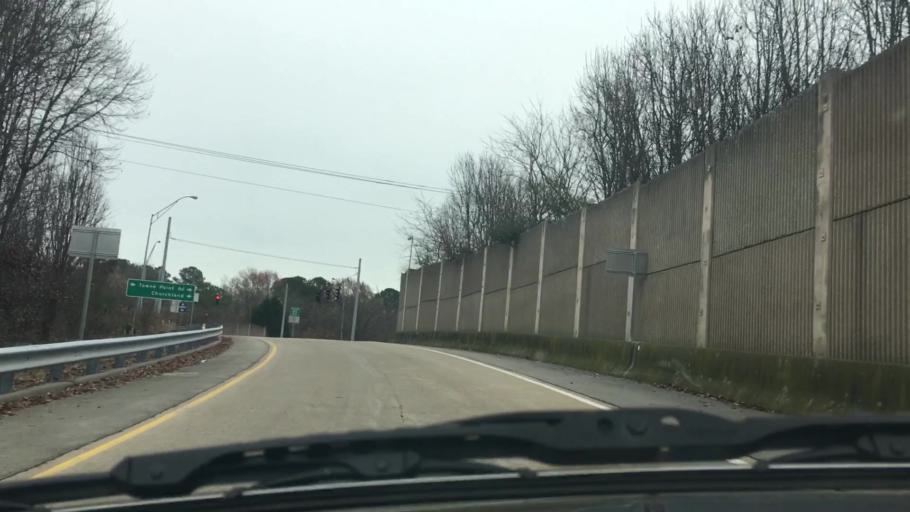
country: US
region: Virginia
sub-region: City of Portsmouth
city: Portsmouth Heights
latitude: 36.8691
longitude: -76.4019
